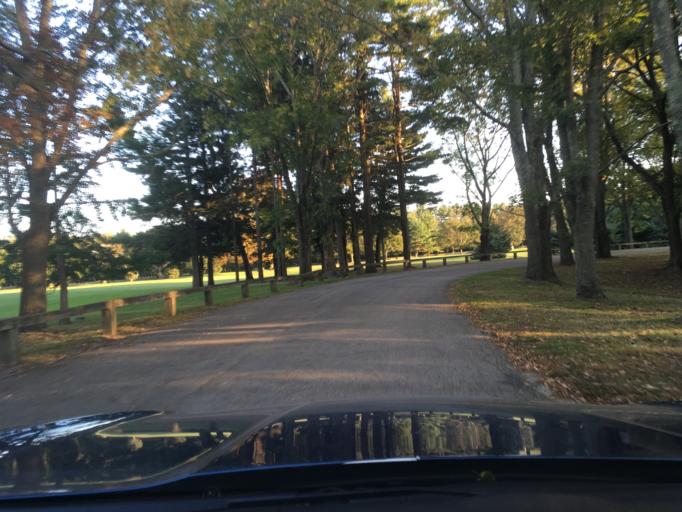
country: US
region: Rhode Island
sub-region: Kent County
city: East Greenwich
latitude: 41.6565
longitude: -71.4373
